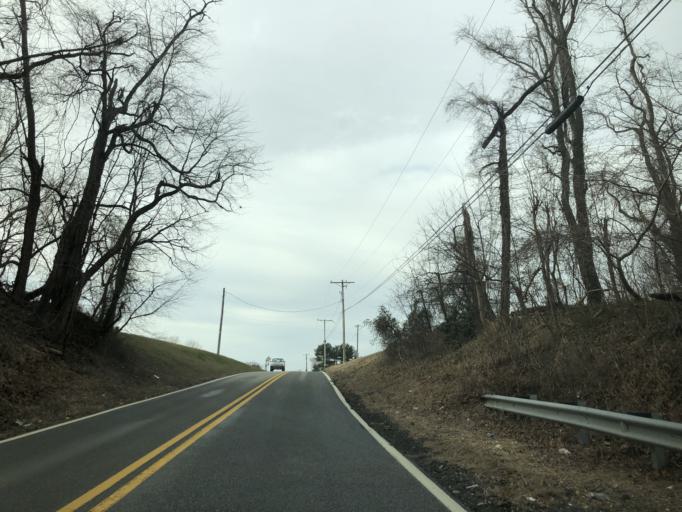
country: US
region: Delaware
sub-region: New Castle County
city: Middletown
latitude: 39.4924
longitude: -75.6900
